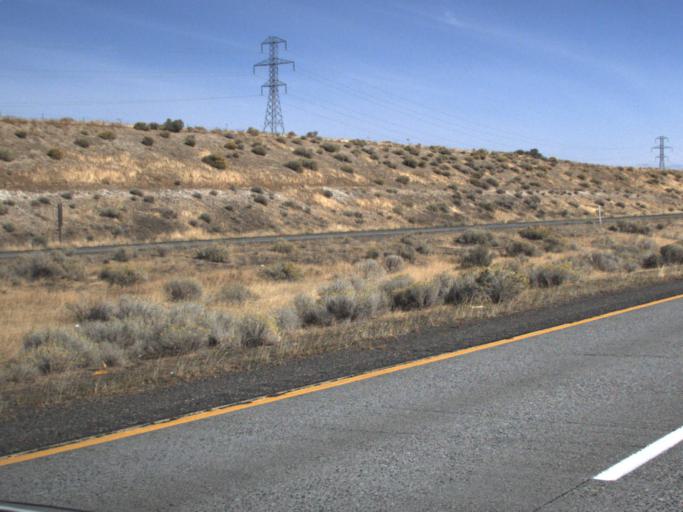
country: US
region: Washington
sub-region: Franklin County
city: West Pasco
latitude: 46.1764
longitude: -119.2308
